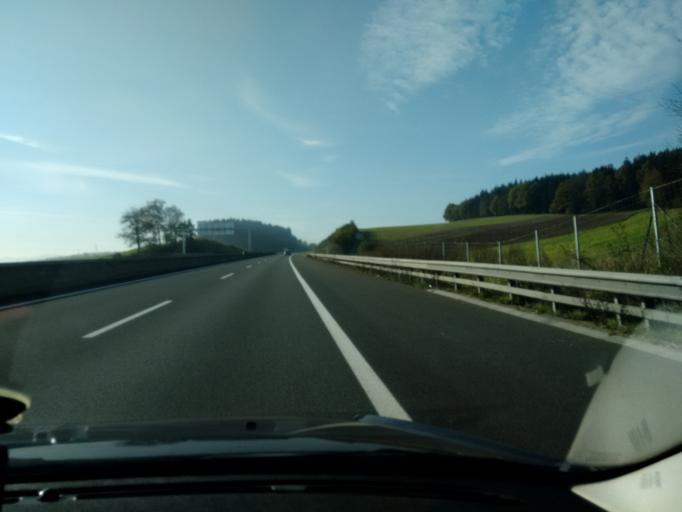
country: AT
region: Upper Austria
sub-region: Wels-Land
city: Bachmanning
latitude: 48.1786
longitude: 13.7712
